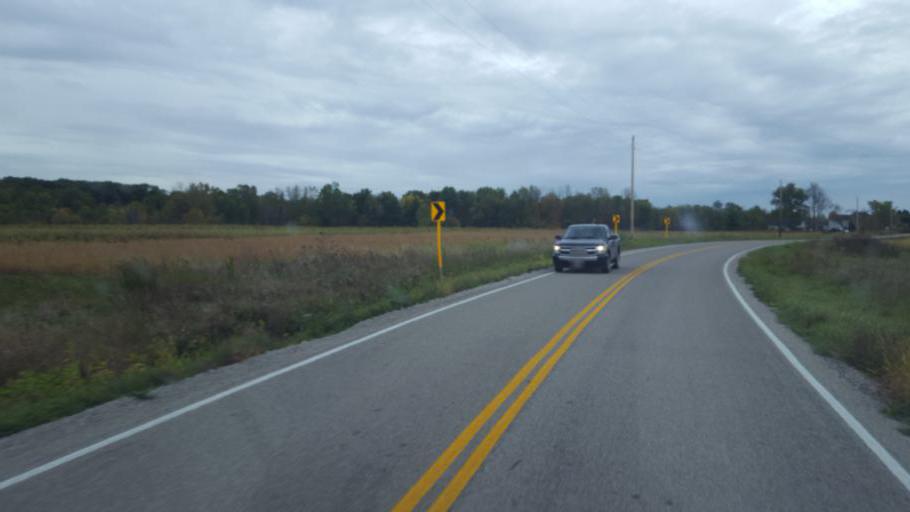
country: US
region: Ohio
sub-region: Huron County
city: Wakeman
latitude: 41.1819
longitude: -82.4313
